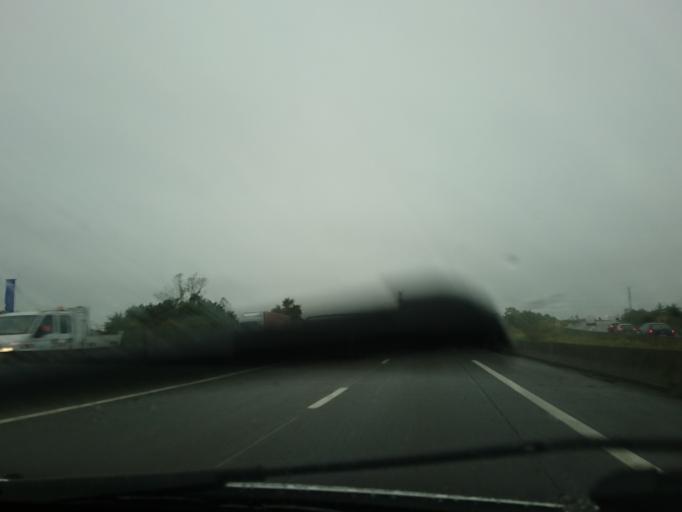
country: FR
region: Brittany
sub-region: Departement du Morbihan
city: Lanester
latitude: 47.7788
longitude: -3.3497
